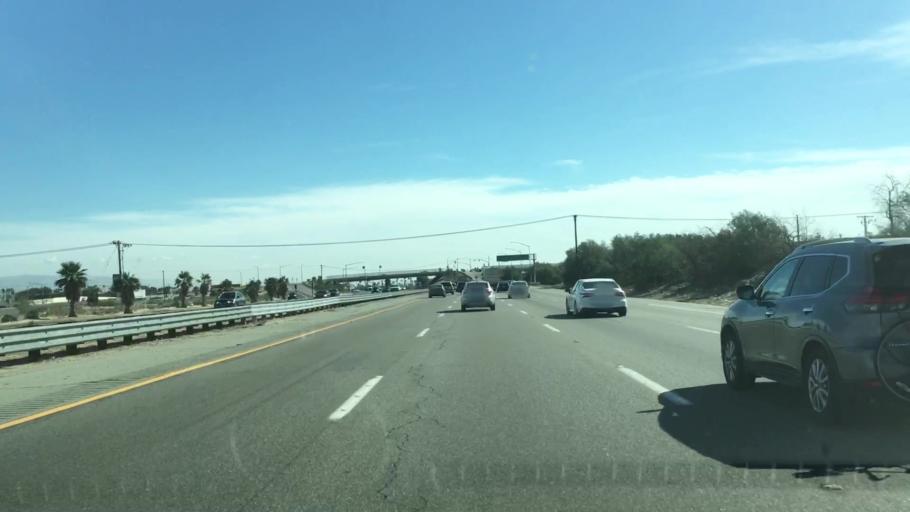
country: US
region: California
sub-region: Riverside County
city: Thousand Palms
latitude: 33.8090
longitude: -116.3936
